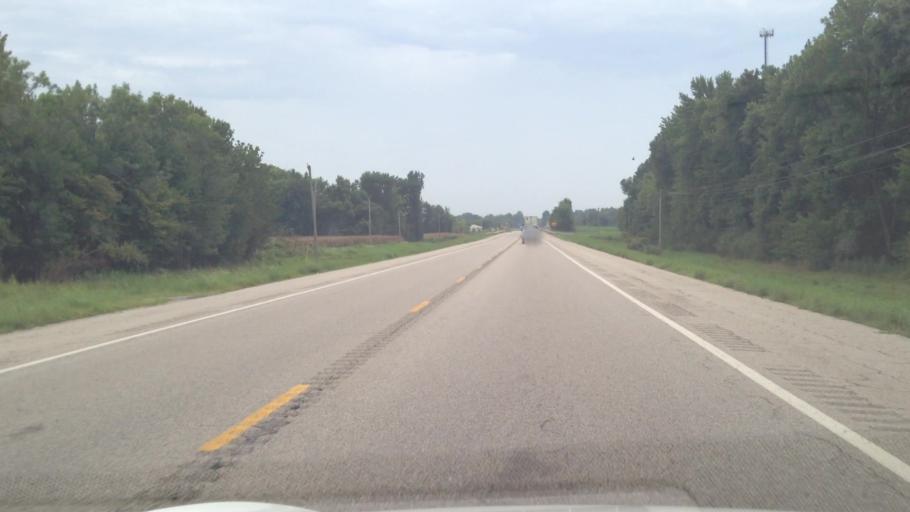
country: US
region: Kansas
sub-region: Cherokee County
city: Galena
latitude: 37.1854
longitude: -94.7046
